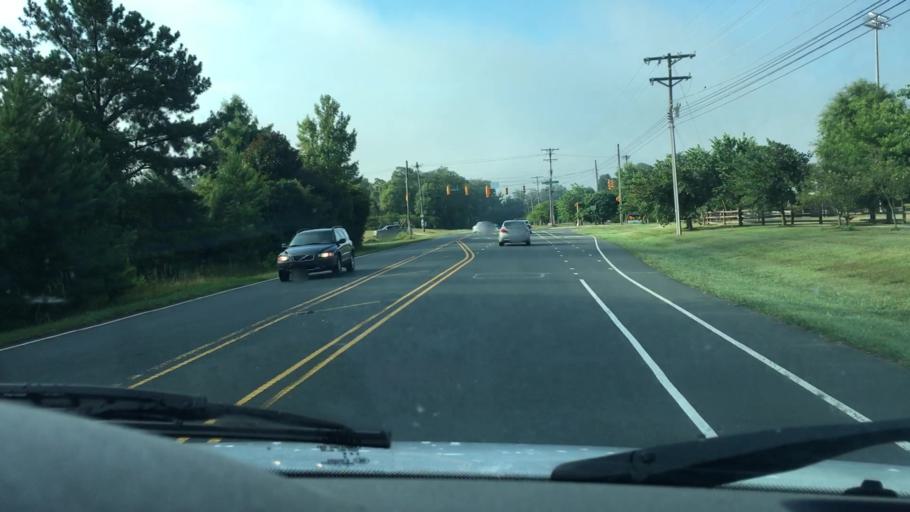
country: US
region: North Carolina
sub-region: Mecklenburg County
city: Huntersville
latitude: 35.4022
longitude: -80.9246
